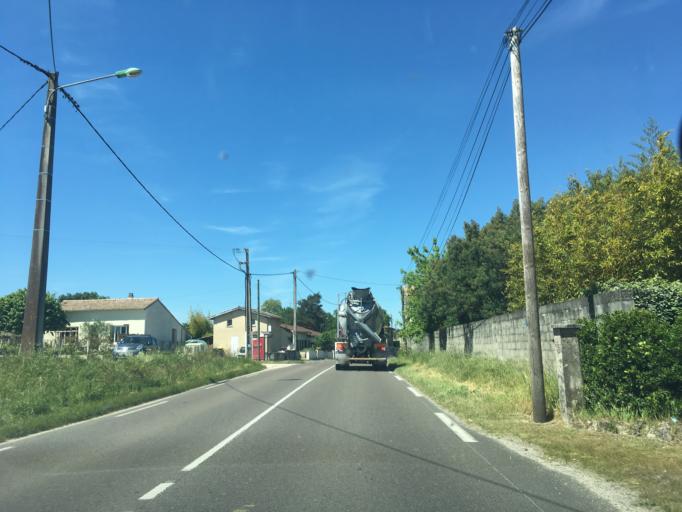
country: FR
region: Aquitaine
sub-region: Departement de la Gironde
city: Listrac-Medoc
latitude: 45.0845
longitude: -0.7964
